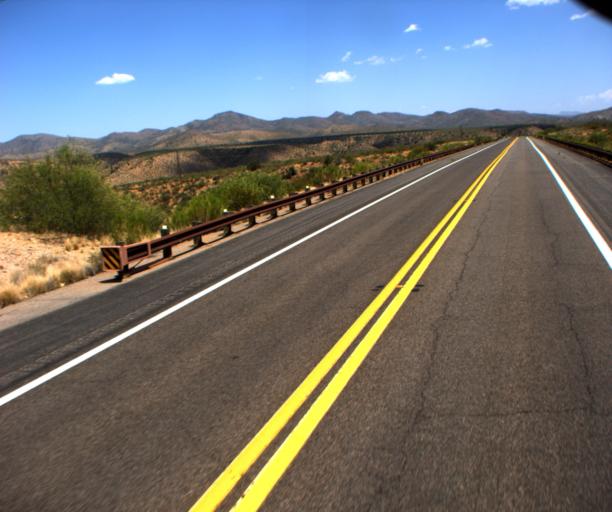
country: US
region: Arizona
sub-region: Gila County
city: Claypool
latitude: 33.4881
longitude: -110.8602
